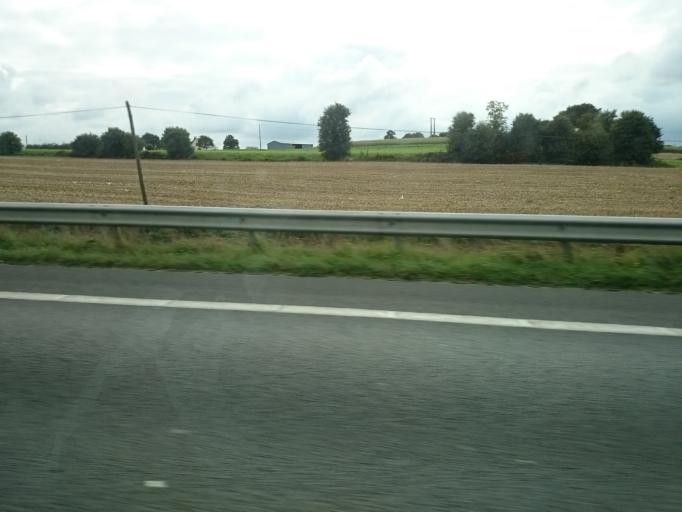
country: FR
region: Brittany
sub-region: Departement des Cotes-d'Armor
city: Lamballe
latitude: 48.4620
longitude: -2.5403
